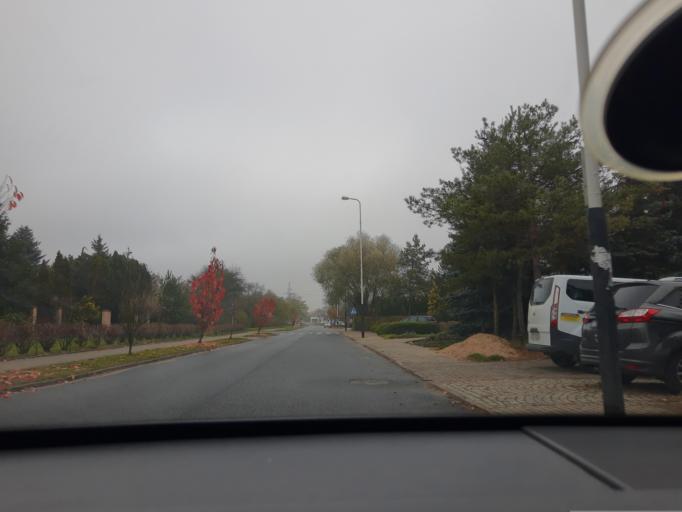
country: PL
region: Lodz Voivodeship
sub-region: Powiat pabianicki
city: Konstantynow Lodzki
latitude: 51.7447
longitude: 19.3777
